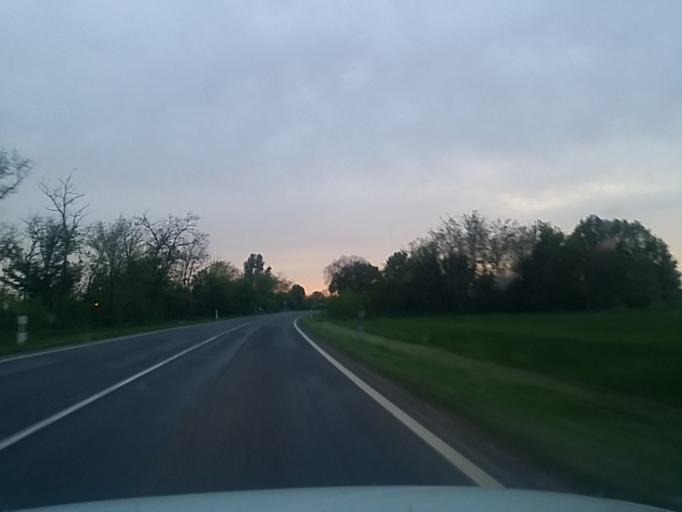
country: HU
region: Bekes
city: Csorvas
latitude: 46.7150
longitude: 20.9392
